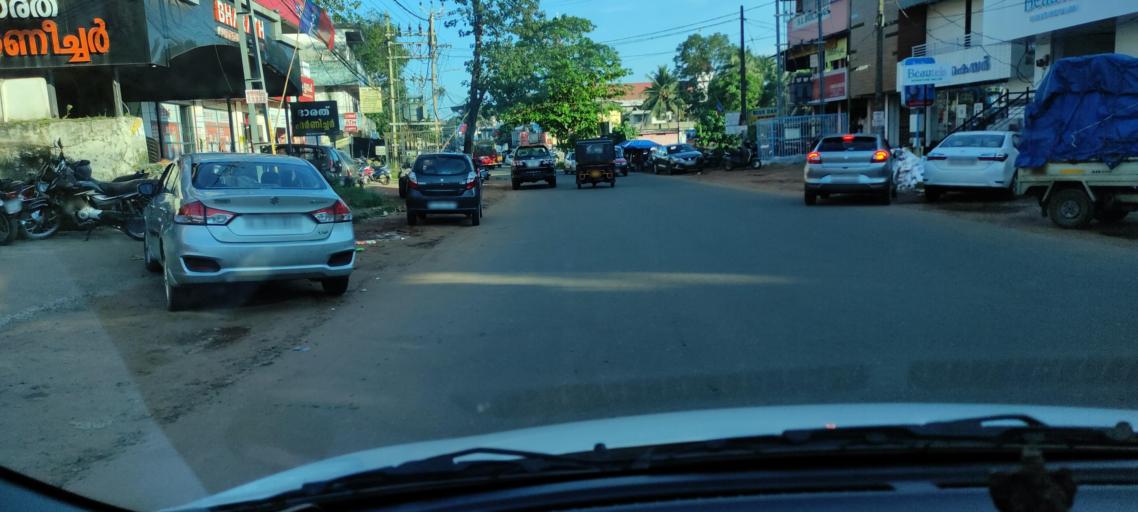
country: IN
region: Kerala
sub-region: Pattanamtitta
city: Adur
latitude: 9.1585
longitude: 76.7255
